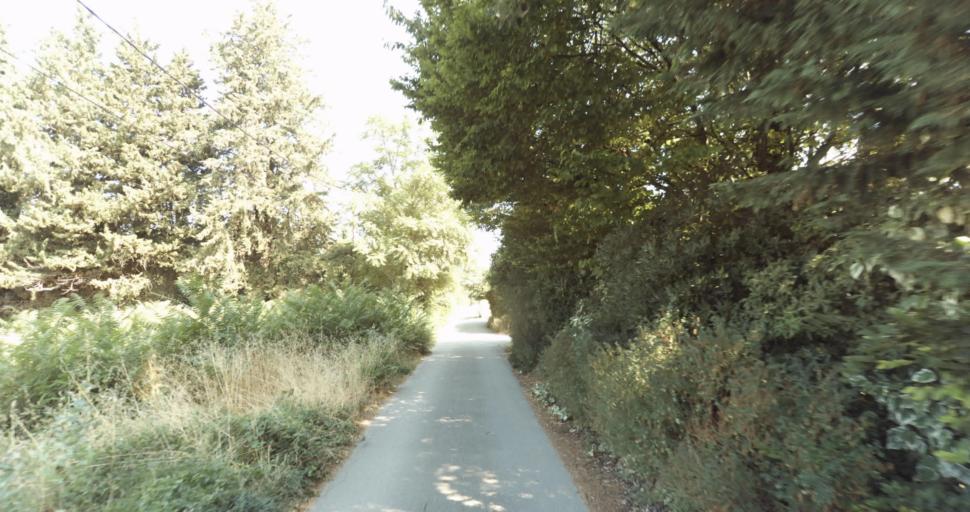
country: FR
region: Provence-Alpes-Cote d'Azur
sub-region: Departement du Vaucluse
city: Monteux
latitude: 44.0258
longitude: 5.0245
